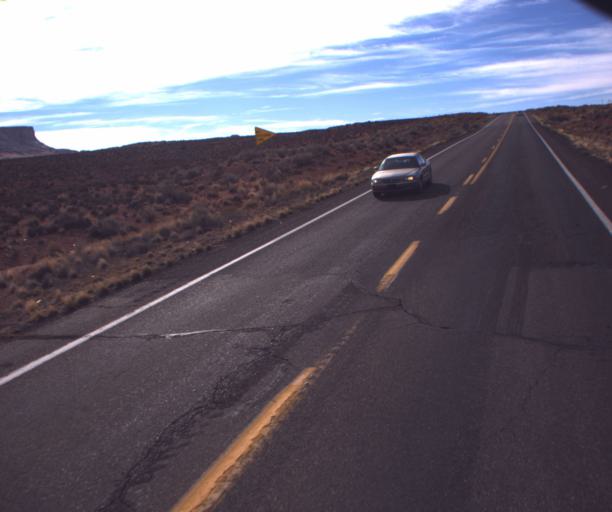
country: US
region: Arizona
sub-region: Coconino County
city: LeChee
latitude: 36.8720
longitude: -111.3421
